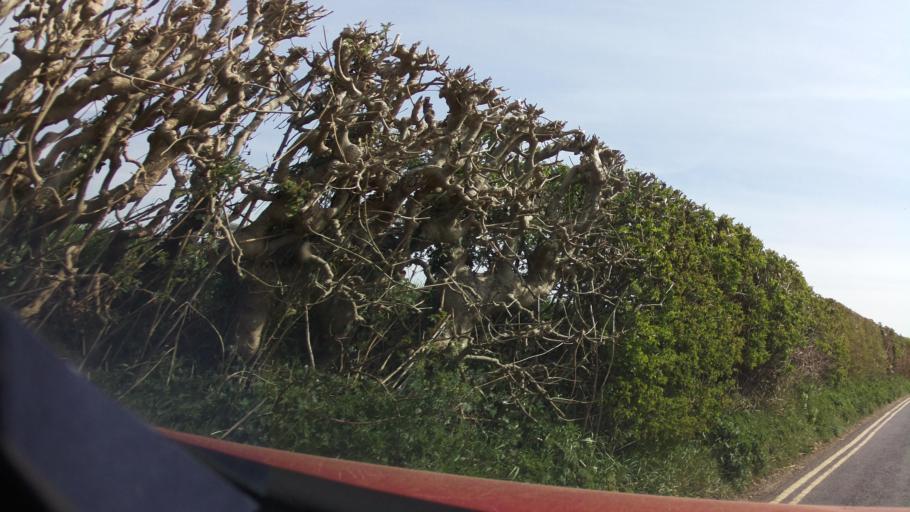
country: GB
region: England
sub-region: Somerset
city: Ilchester
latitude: 51.0161
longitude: -2.6296
